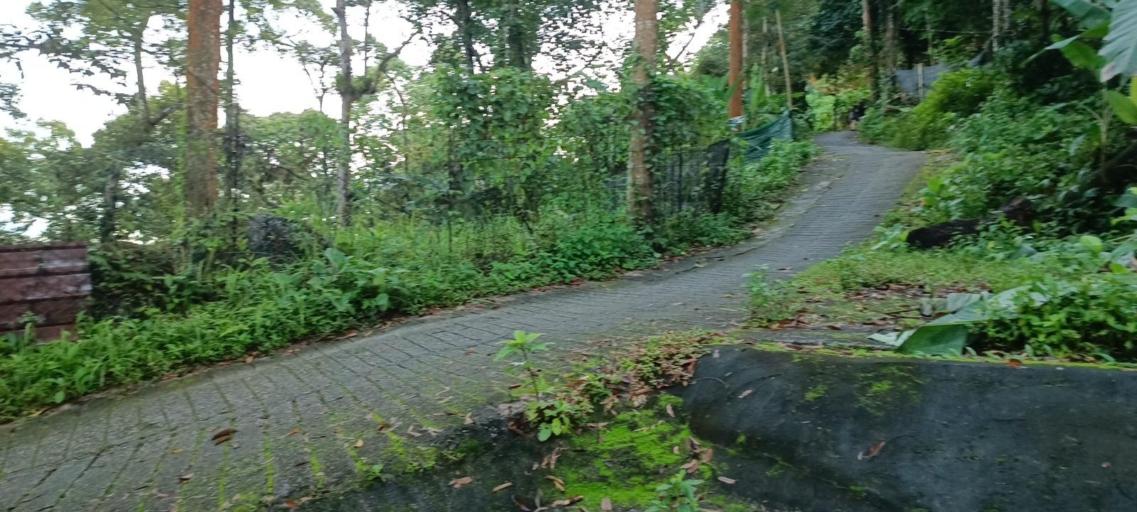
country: MY
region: Penang
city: Bukit Mertajam
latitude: 5.3732
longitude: 100.4776
